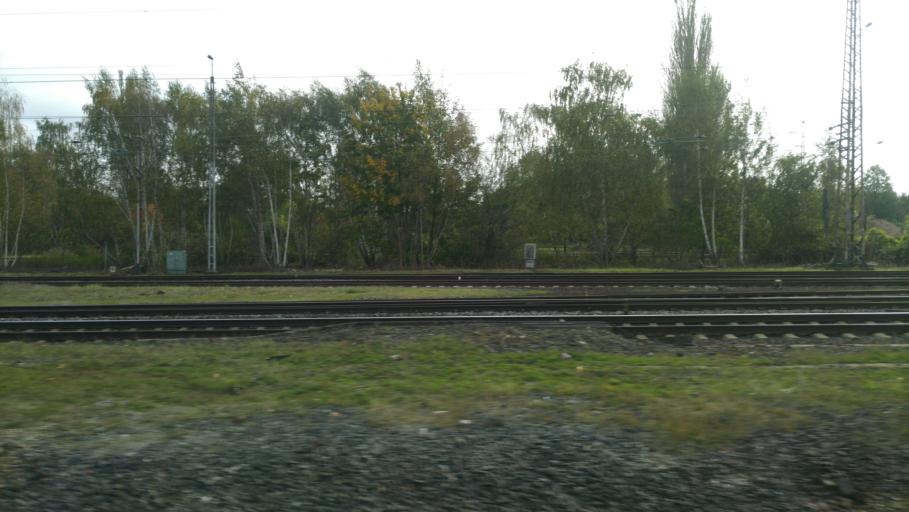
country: DE
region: Lower Saxony
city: Elze
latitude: 52.1189
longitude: 9.7461
